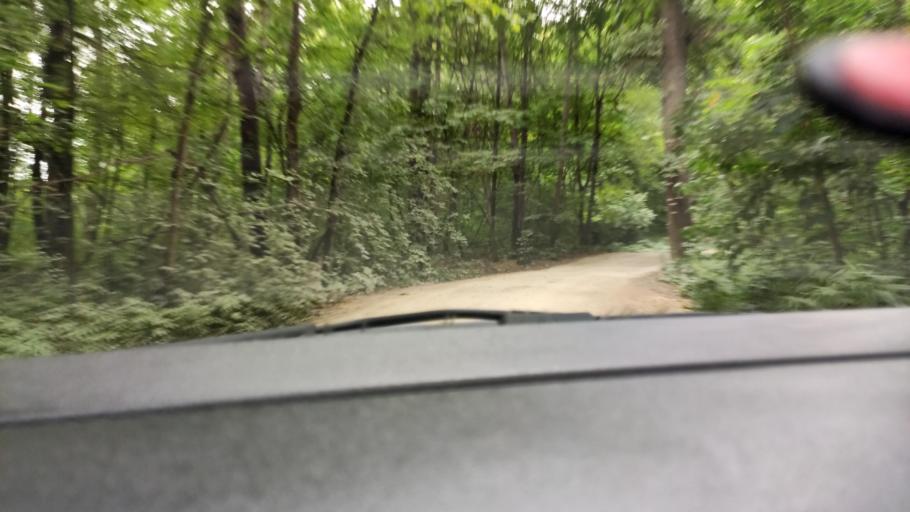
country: RU
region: Voronezj
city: Ramon'
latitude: 51.8897
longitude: 39.3520
